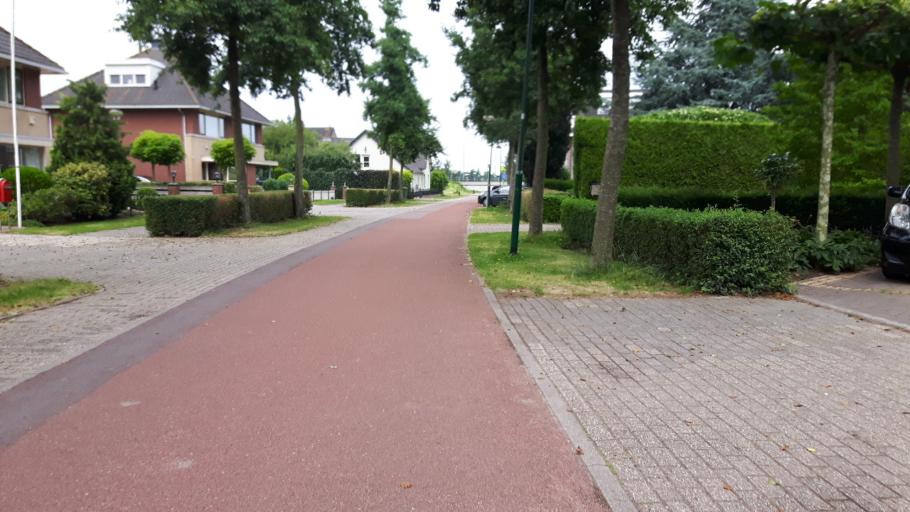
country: NL
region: Utrecht
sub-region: Gemeente Houten
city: Houten
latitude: 52.0246
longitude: 5.1845
